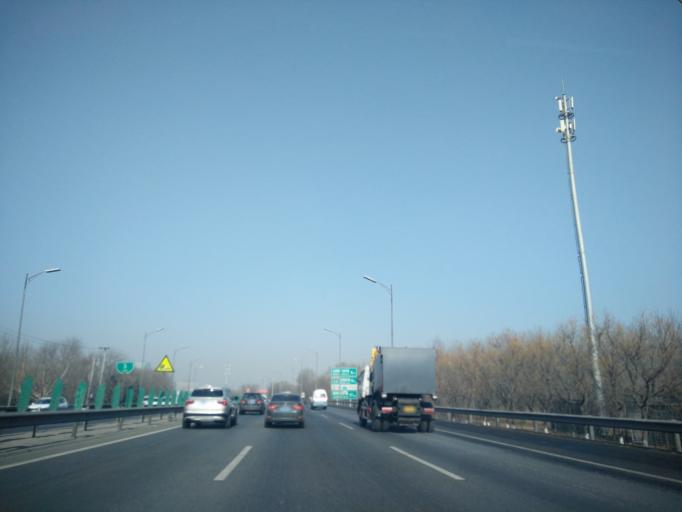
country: CN
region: Beijing
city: Wangjing
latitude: 40.0093
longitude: 116.4828
